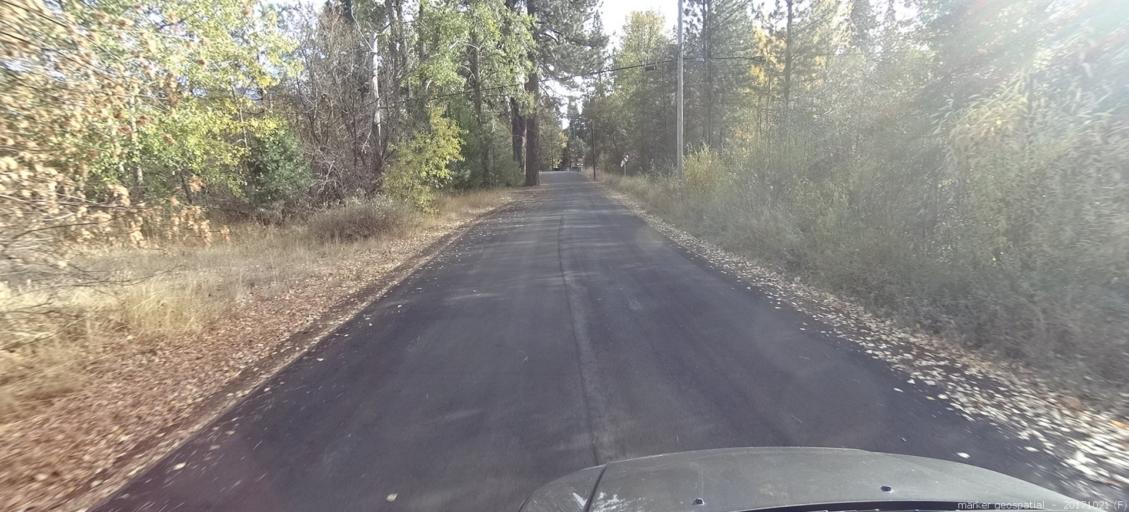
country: US
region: California
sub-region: Shasta County
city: Burney
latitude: 40.8723
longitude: -121.6977
